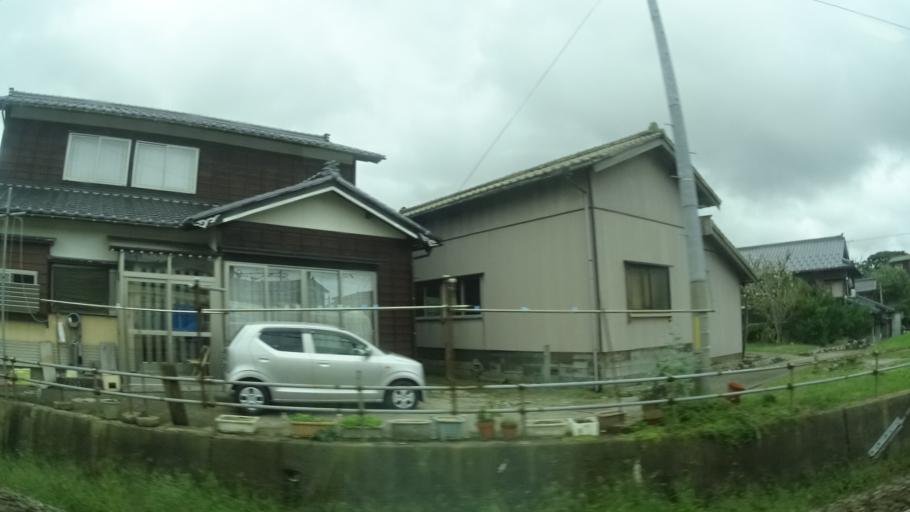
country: JP
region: Niigata
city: Murakami
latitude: 38.5172
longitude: 139.5350
